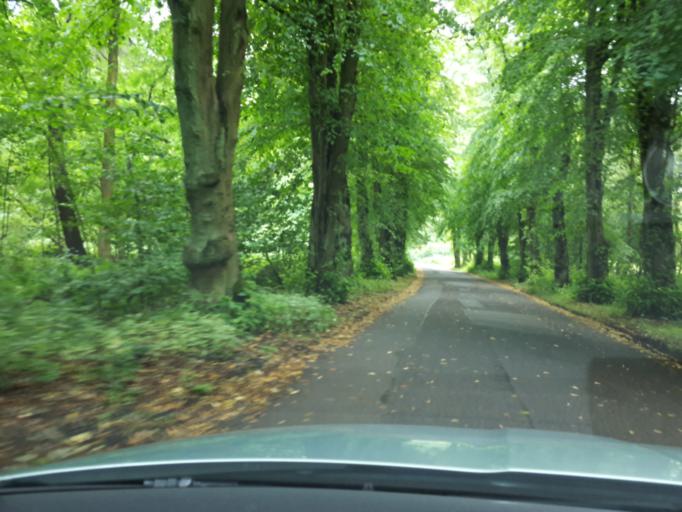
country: GB
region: Scotland
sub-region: Falkirk
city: Polmont
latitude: 55.9644
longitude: -3.6679
